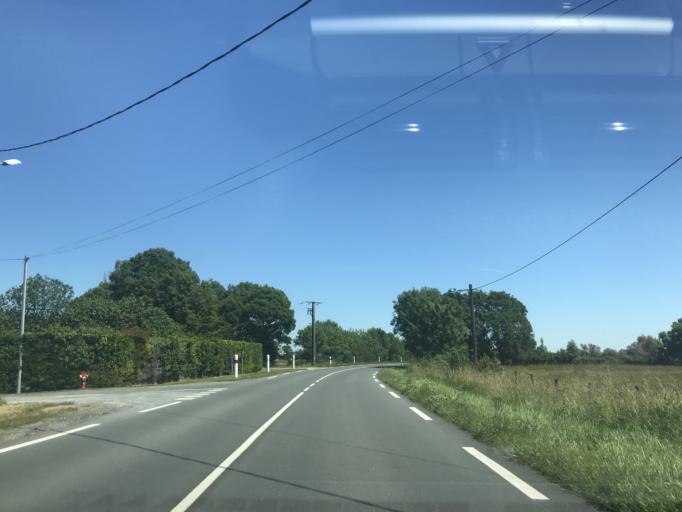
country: FR
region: Poitou-Charentes
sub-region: Departement de la Charente-Maritime
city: Meschers-sur-Gironde
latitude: 45.5620
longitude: -0.9376
